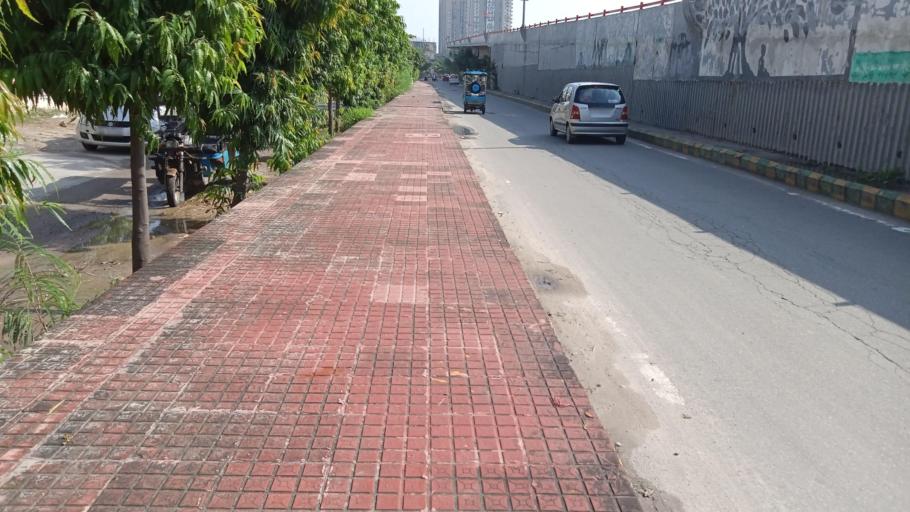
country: IN
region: Uttar Pradesh
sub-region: Ghaziabad
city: Ghaziabad
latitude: 28.6606
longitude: 77.3746
